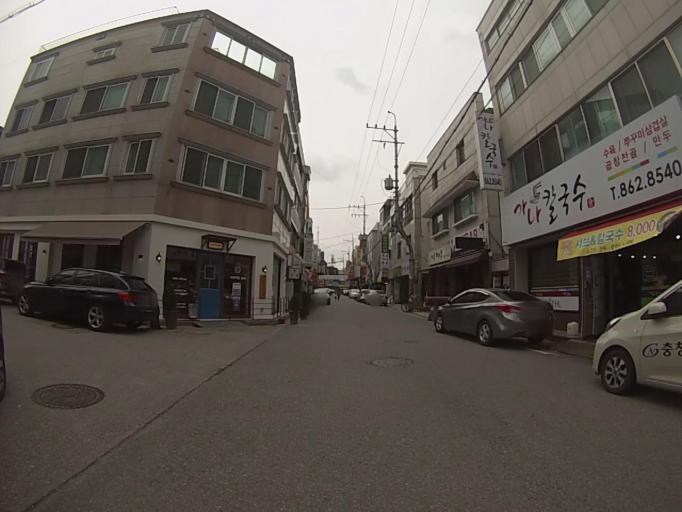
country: KR
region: Daejeon
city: Songgang-dong
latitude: 36.3636
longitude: 127.3581
